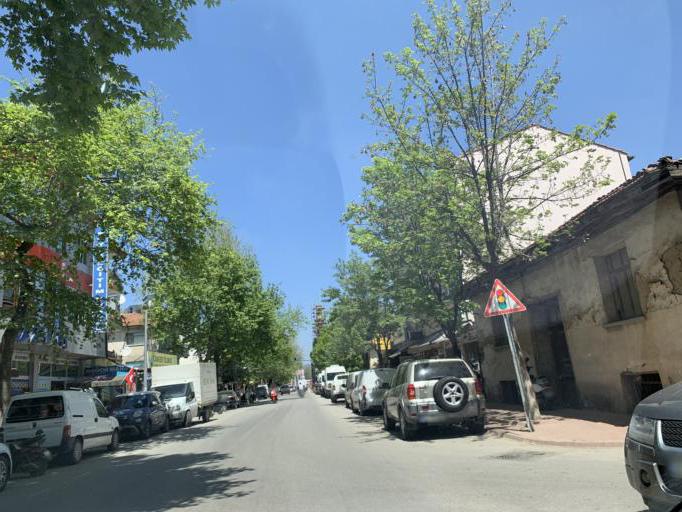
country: TR
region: Bursa
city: Iznik
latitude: 40.4267
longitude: 29.7195
